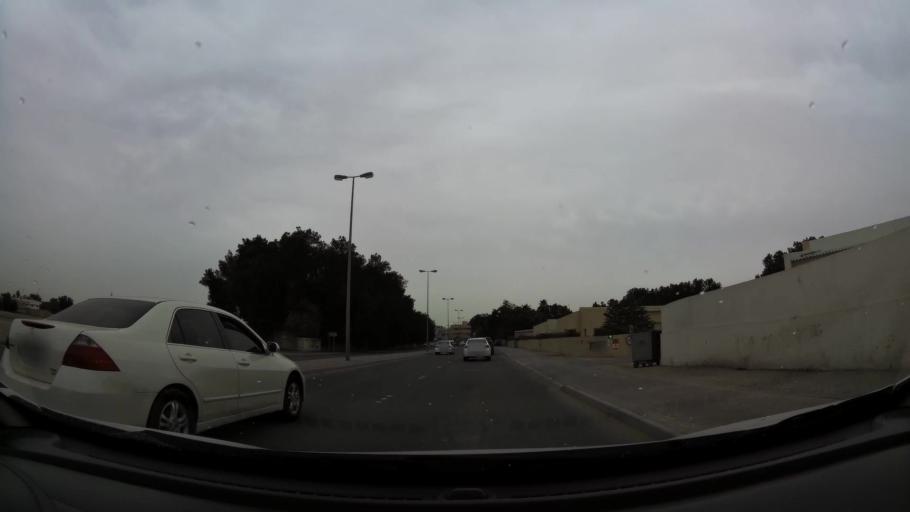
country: BH
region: Manama
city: Jidd Hafs
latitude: 26.2082
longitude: 50.5339
